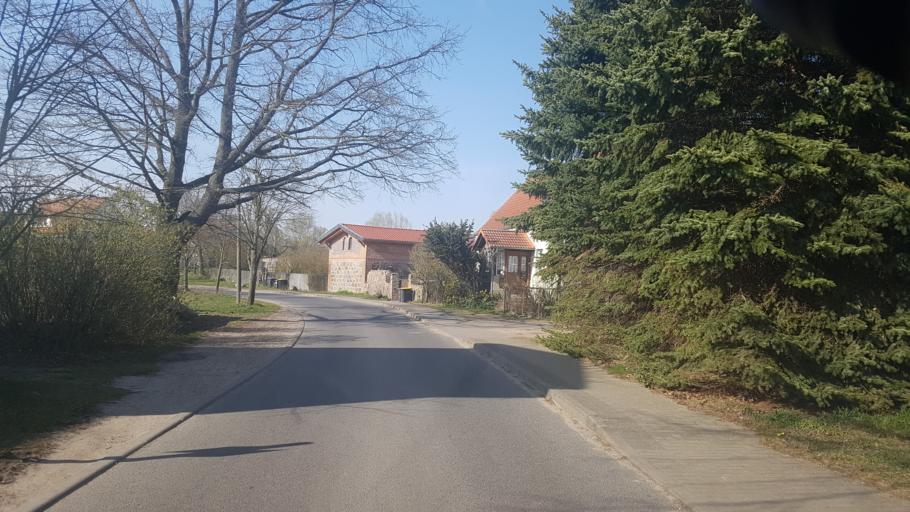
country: DE
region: Brandenburg
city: Gerswalde
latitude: 53.1762
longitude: 13.7741
